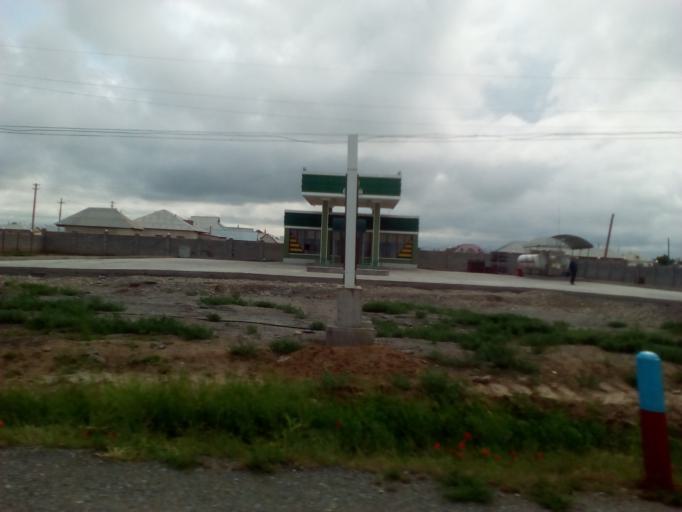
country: KZ
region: Ongtustik Qazaqstan
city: Sholaqqkorghan
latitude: 43.7519
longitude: 69.1947
